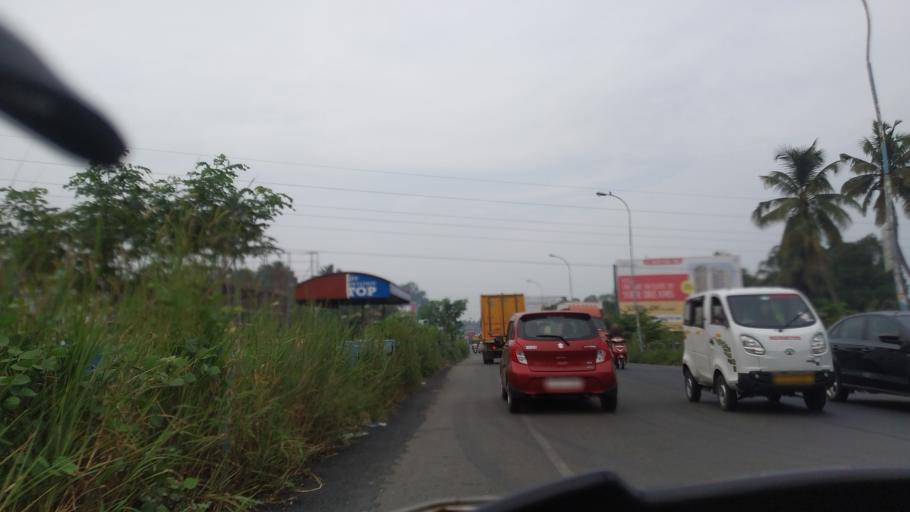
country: IN
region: Kerala
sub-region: Ernakulam
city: Elur
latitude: 10.0396
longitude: 76.3009
